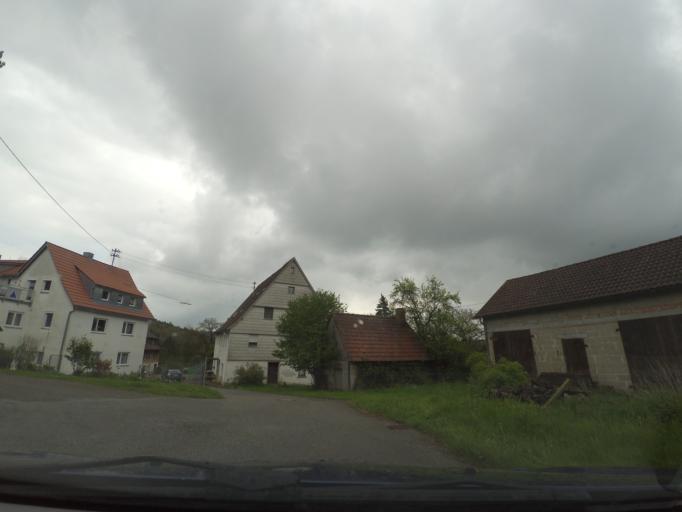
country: DE
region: Baden-Wuerttemberg
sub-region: Regierungsbezirk Stuttgart
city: Murrhardt
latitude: 49.0165
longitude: 9.5707
